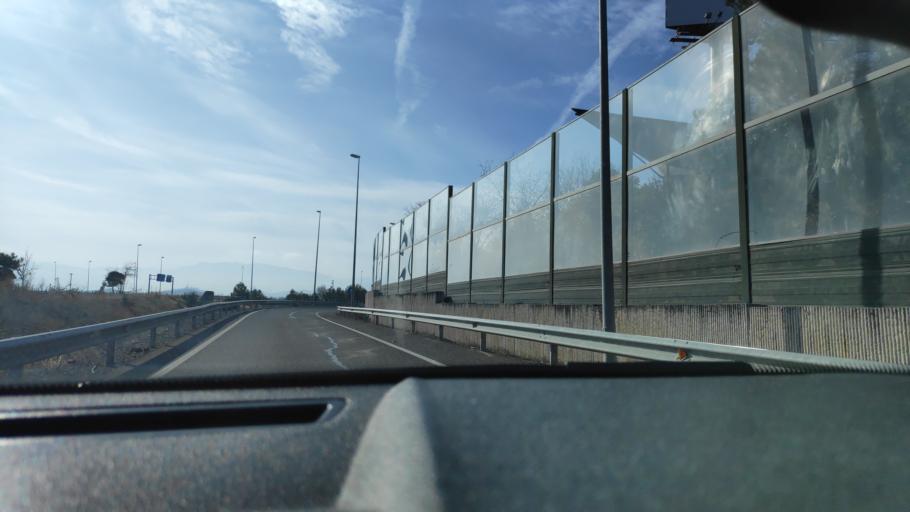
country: ES
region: Andalusia
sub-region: Provincia de Jaen
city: Jaen
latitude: 37.8179
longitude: -3.7676
